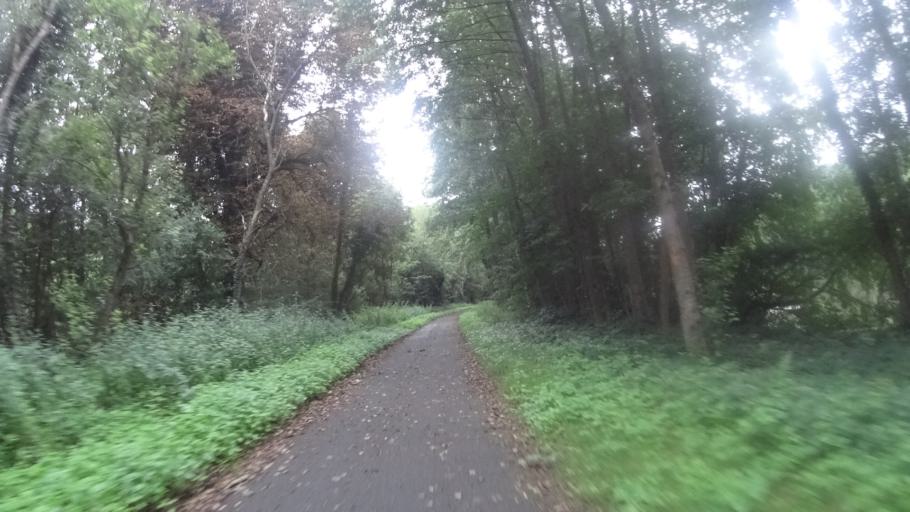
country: FR
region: Lorraine
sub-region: Departement de Meurthe-et-Moselle
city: Velaine-en-Haye
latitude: 48.6614
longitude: 6.0173
